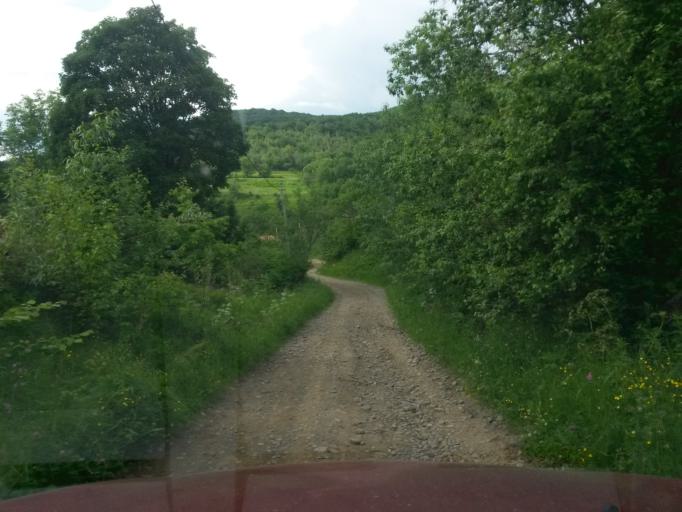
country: UA
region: Zakarpattia
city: Velykyi Bereznyi
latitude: 48.8997
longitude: 22.5274
